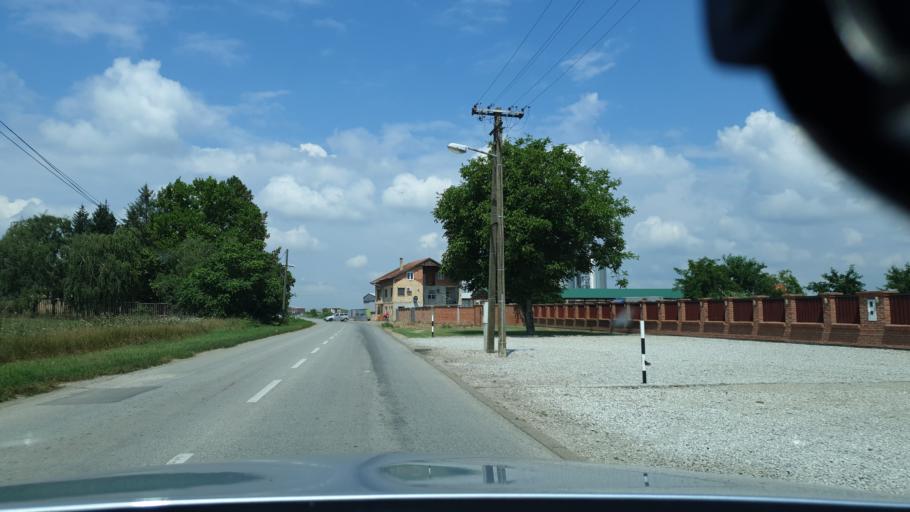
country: RS
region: Autonomna Pokrajina Vojvodina
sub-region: Juznobacki Okrug
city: Kovilj
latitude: 45.2410
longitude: 20.0256
